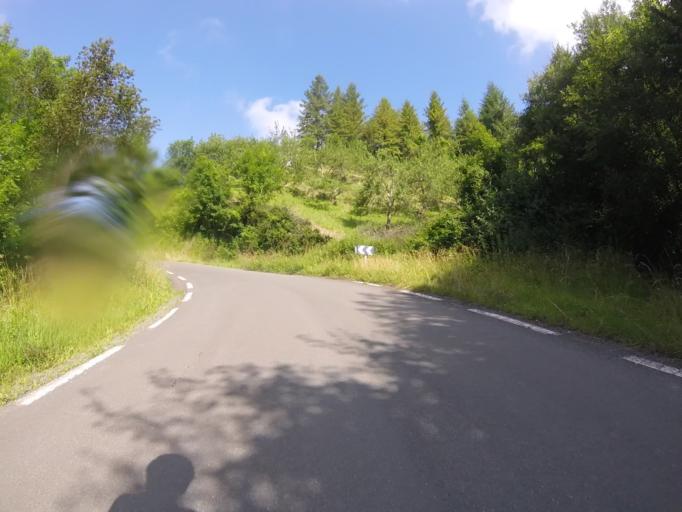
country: ES
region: Basque Country
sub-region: Provincia de Guipuzcoa
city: Beasain
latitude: 43.0815
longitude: -2.2238
